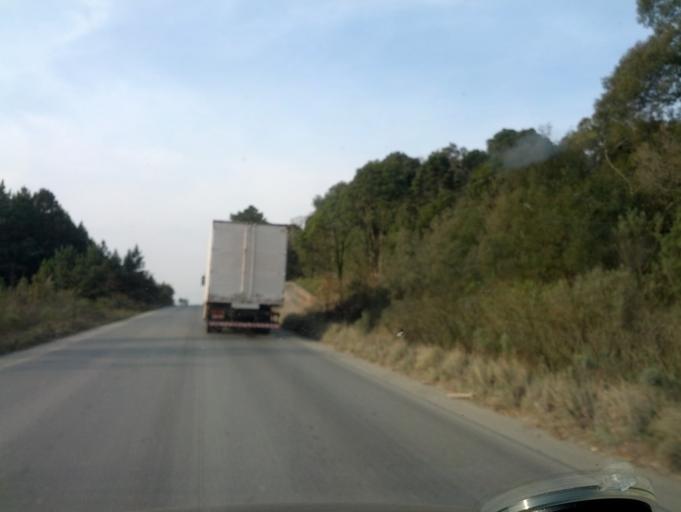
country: BR
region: Santa Catarina
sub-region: Otacilio Costa
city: Otacilio Costa
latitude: -27.5265
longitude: -50.1383
